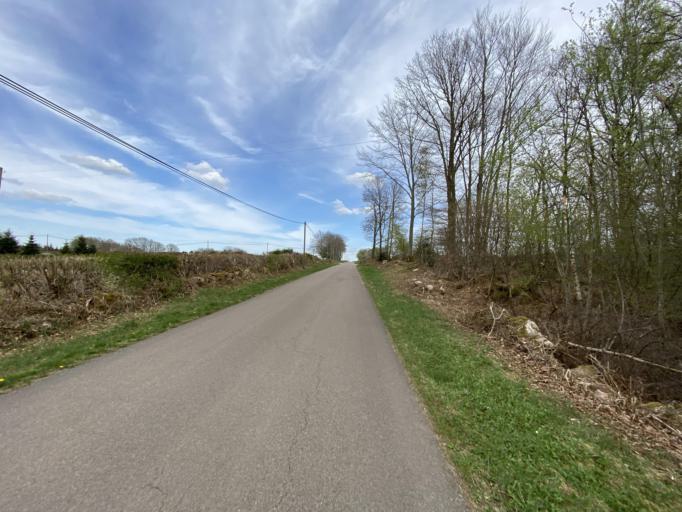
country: FR
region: Bourgogne
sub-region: Departement de la Cote-d'Or
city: Saulieu
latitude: 47.3195
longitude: 4.0692
